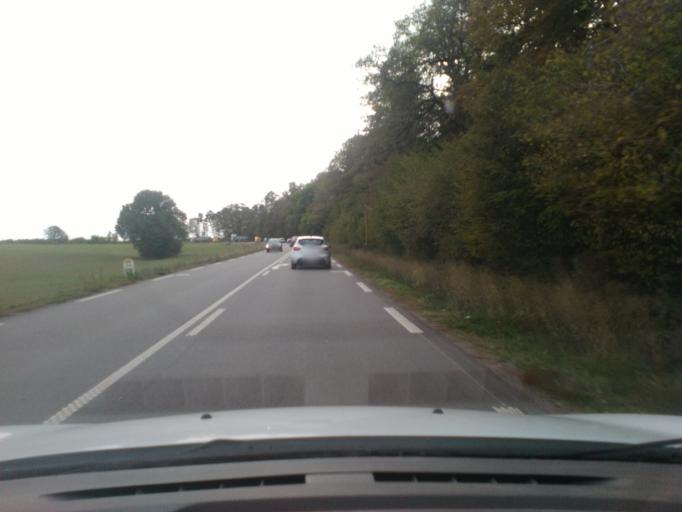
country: FR
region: Lorraine
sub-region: Departement des Vosges
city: Aydoilles
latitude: 48.2787
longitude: 6.5651
